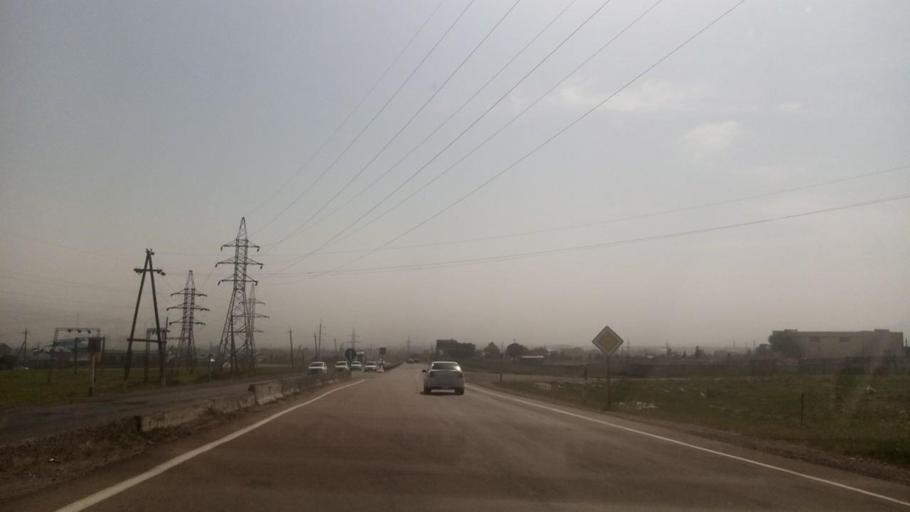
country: UZ
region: Toshkent
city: Angren
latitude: 41.0345
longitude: 70.1425
